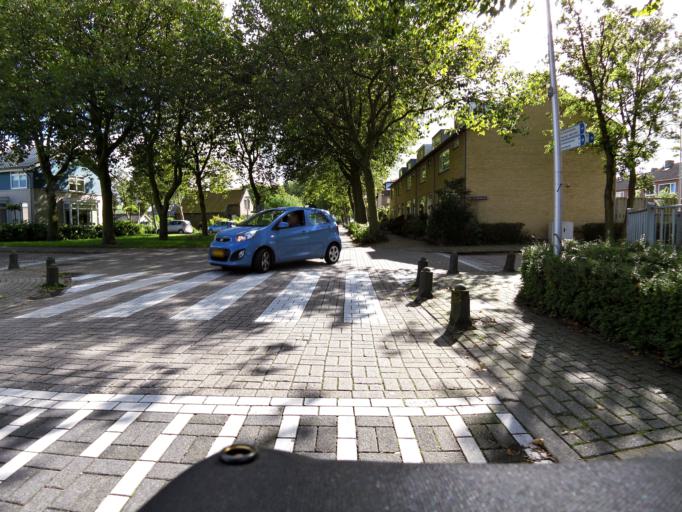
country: NL
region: South Holland
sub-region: Gemeente Delft
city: Delft
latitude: 51.9751
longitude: 4.3177
